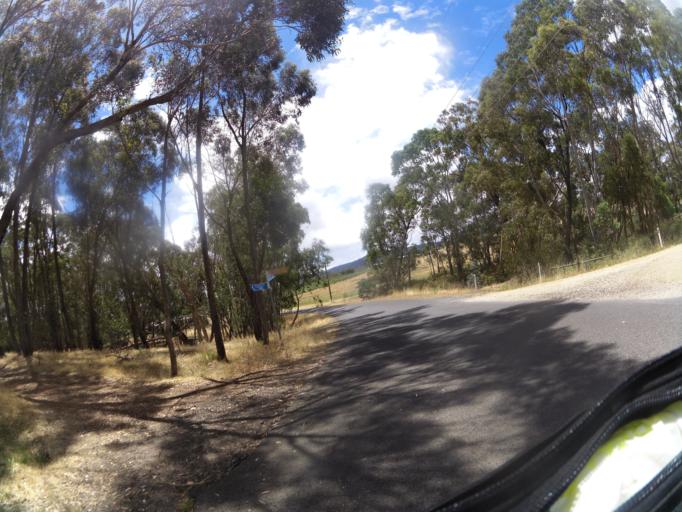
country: AU
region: Victoria
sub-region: Mount Alexander
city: Castlemaine
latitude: -37.0204
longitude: 144.2507
